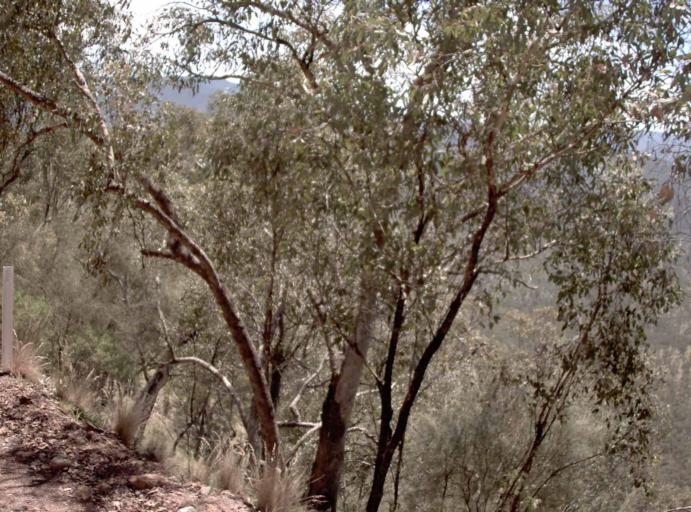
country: AU
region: New South Wales
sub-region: Snowy River
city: Jindabyne
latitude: -36.9944
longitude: 148.3024
